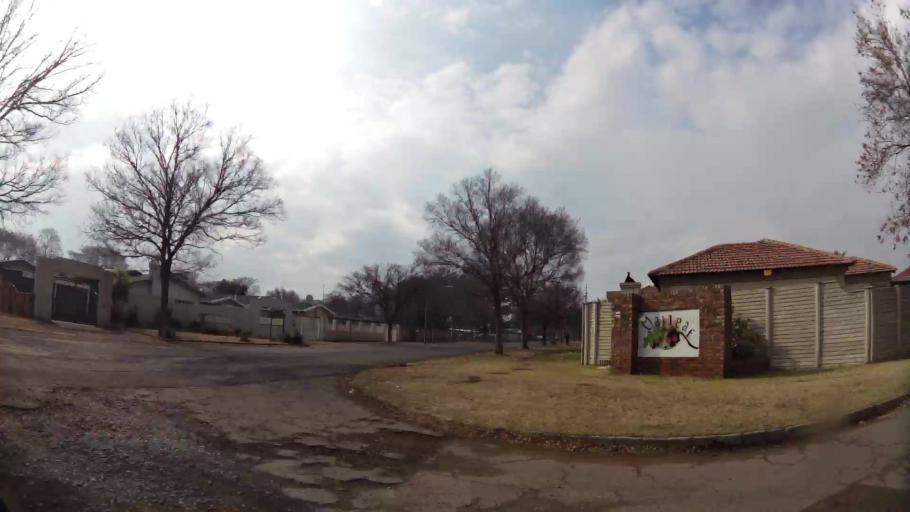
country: ZA
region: Gauteng
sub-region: Sedibeng District Municipality
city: Vanderbijlpark
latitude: -26.6890
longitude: 27.8379
